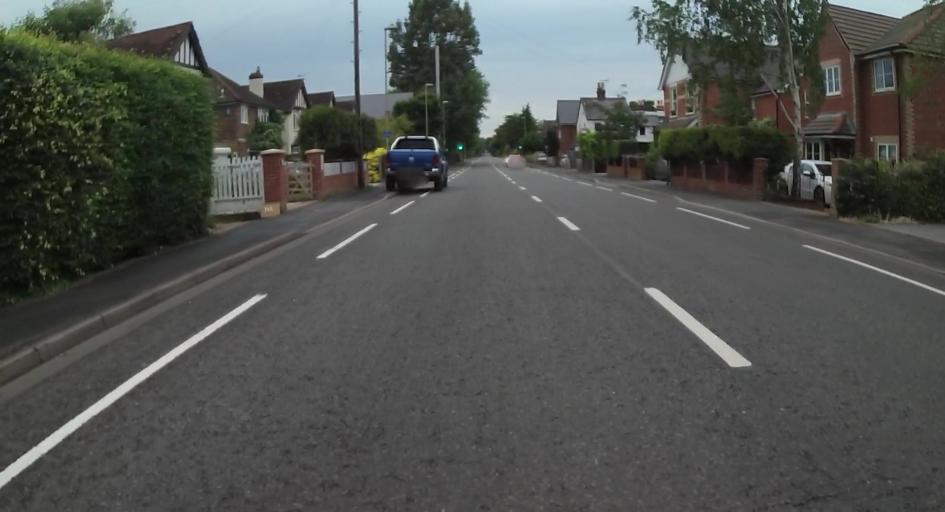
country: GB
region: England
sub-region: Hampshire
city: Fleet
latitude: 51.2788
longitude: -0.8253
